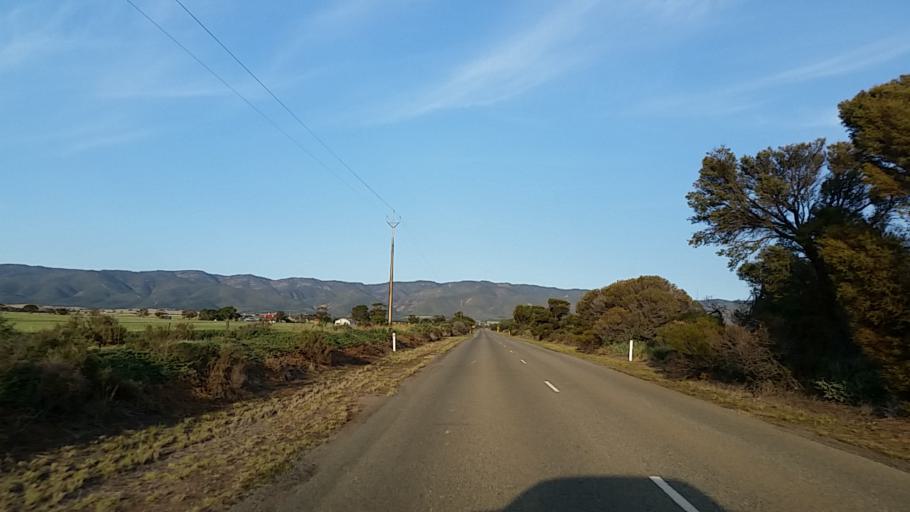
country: AU
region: South Australia
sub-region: Port Pirie City and Dists
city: Port Pirie
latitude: -33.1040
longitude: 138.0600
